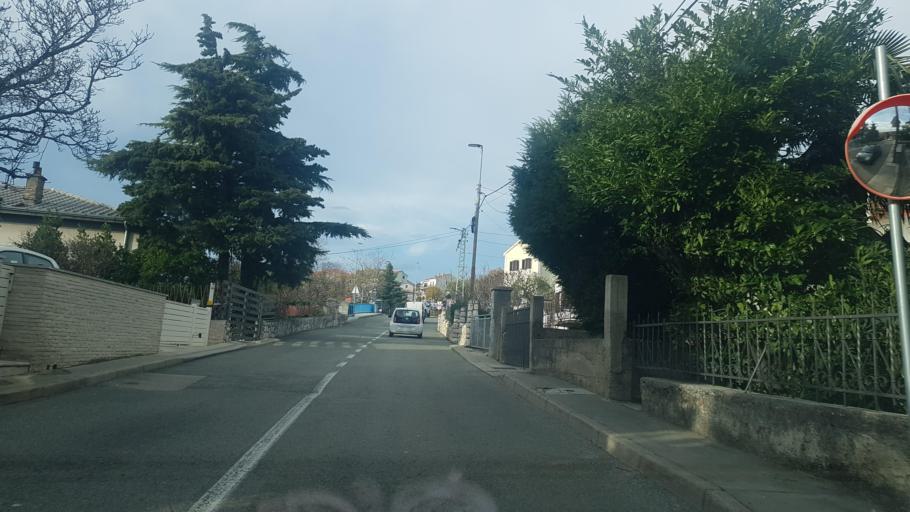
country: HR
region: Primorsko-Goranska
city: Skrljevo
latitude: 45.3089
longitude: 14.4896
